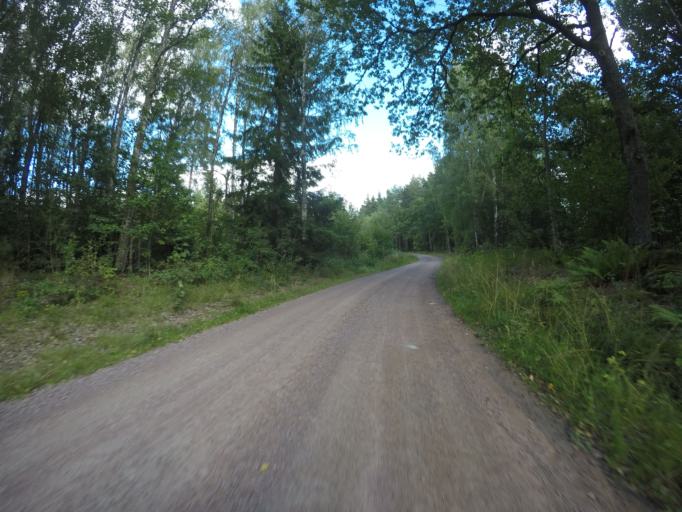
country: SE
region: Vaestmanland
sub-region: Hallstahammars Kommun
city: Kolback
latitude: 59.4917
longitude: 16.1946
